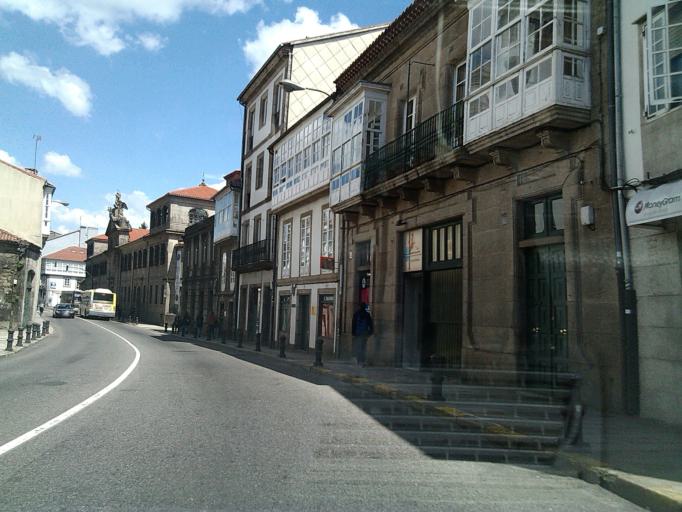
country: ES
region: Galicia
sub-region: Provincia da Coruna
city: Santiago de Compostela
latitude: 42.8780
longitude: -8.5417
